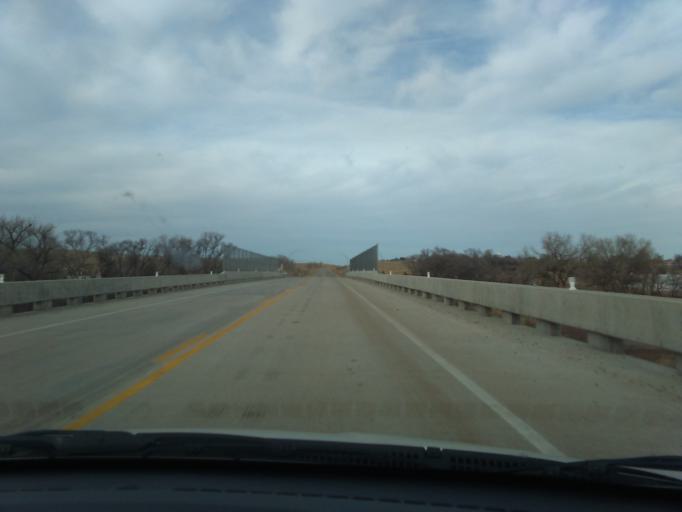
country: US
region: Nebraska
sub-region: Dundy County
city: Benkelman
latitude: 40.0417
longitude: -101.5434
